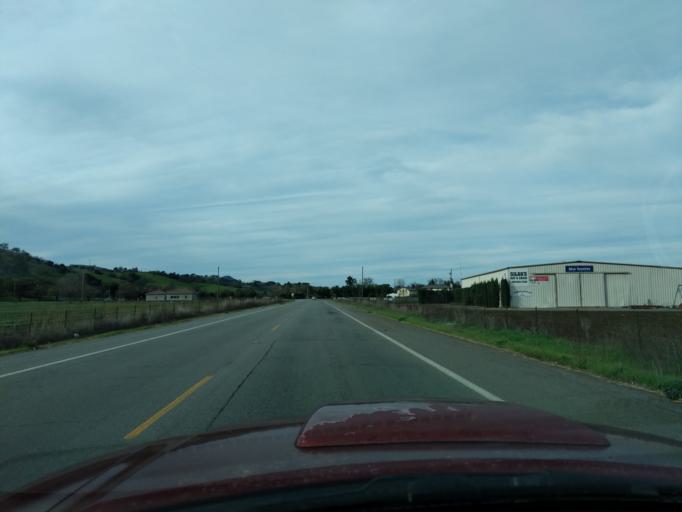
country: US
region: California
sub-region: Santa Clara County
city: San Martin
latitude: 37.0667
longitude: -121.6142
